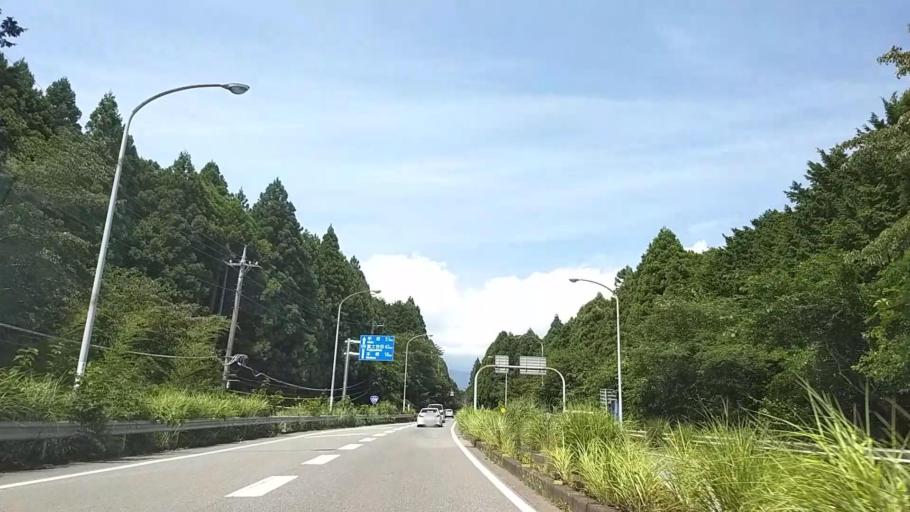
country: JP
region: Shizuoka
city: Fujinomiya
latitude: 35.3287
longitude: 138.5864
